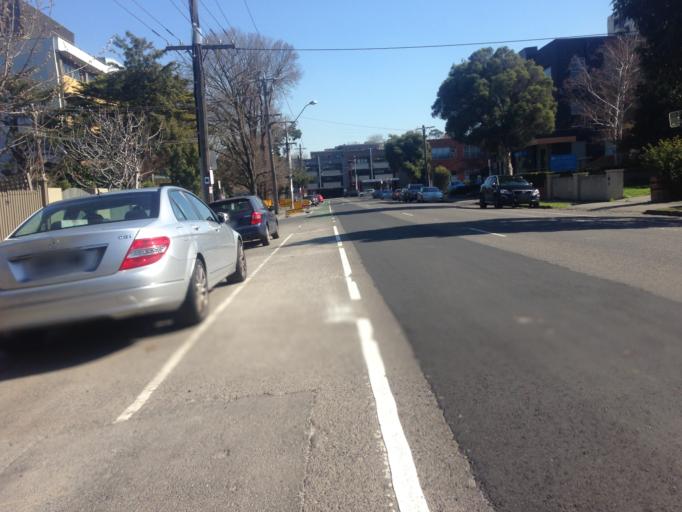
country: AU
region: Victoria
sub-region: Boroondara
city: Kew
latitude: -37.8091
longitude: 145.0303
